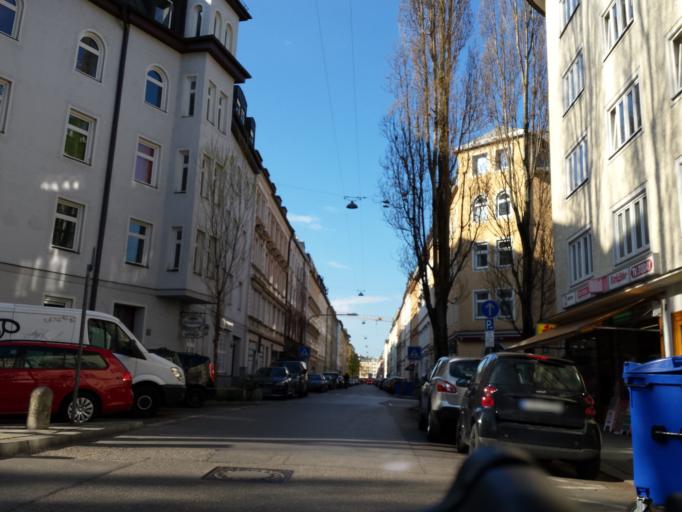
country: DE
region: Bavaria
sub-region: Upper Bavaria
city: Munich
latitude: 48.1317
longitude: 11.5796
